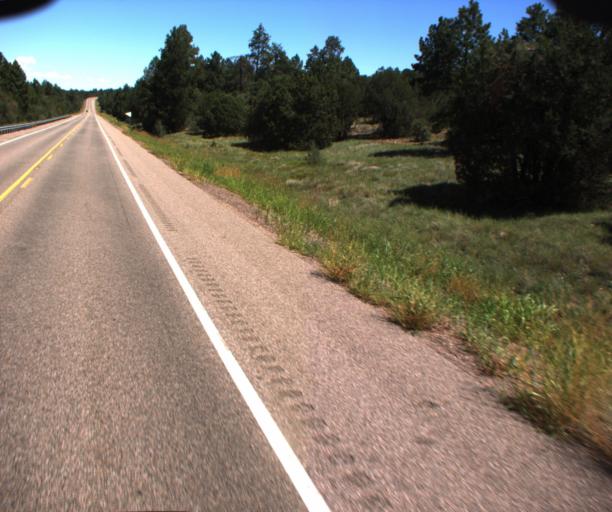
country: US
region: Arizona
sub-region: Gila County
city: San Carlos
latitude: 33.6821
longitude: -110.5723
